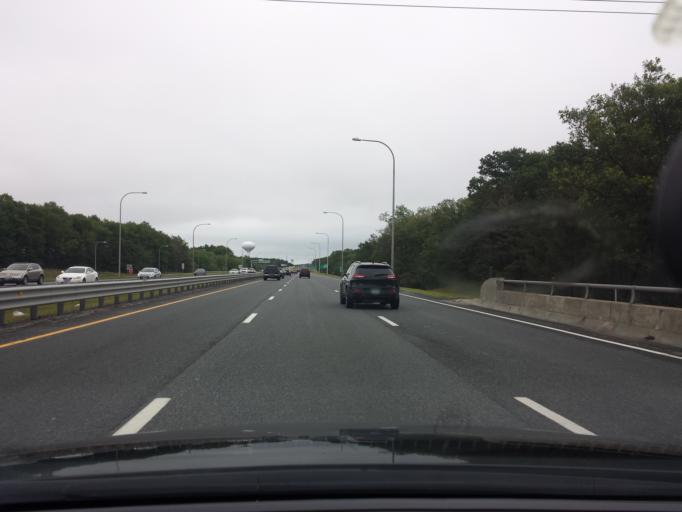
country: US
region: Rhode Island
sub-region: Kent County
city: West Warwick
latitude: 41.6527
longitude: -71.5751
